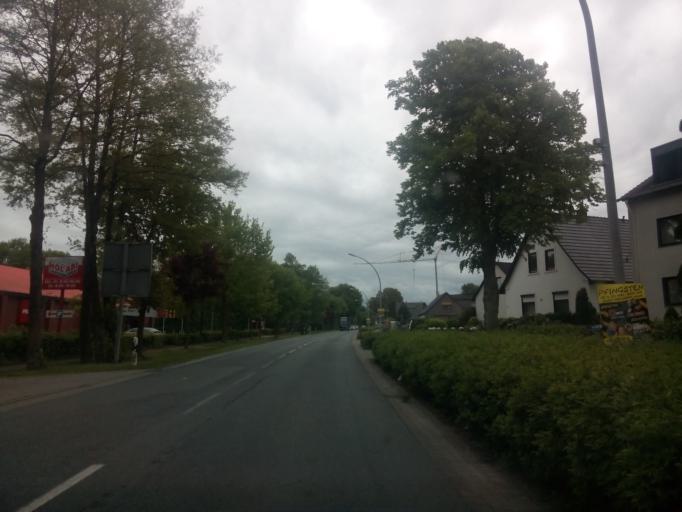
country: DE
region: Lower Saxony
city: Schwanewede
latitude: 53.2313
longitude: 8.5951
